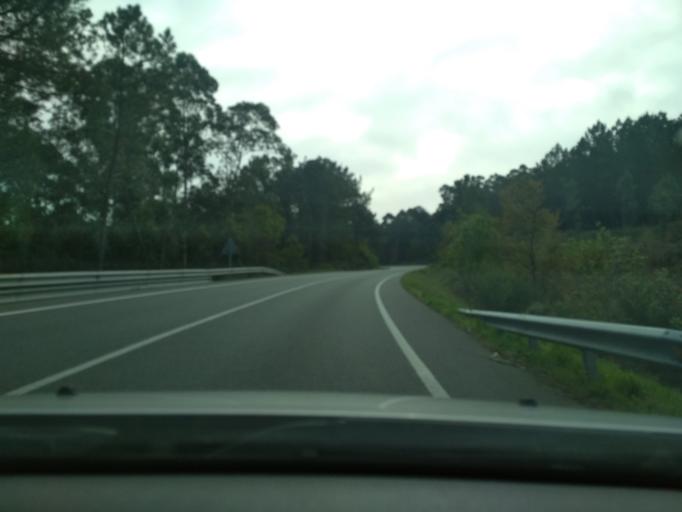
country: ES
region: Galicia
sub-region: Provincia de Pontevedra
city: Catoira
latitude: 42.6530
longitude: -8.6967
